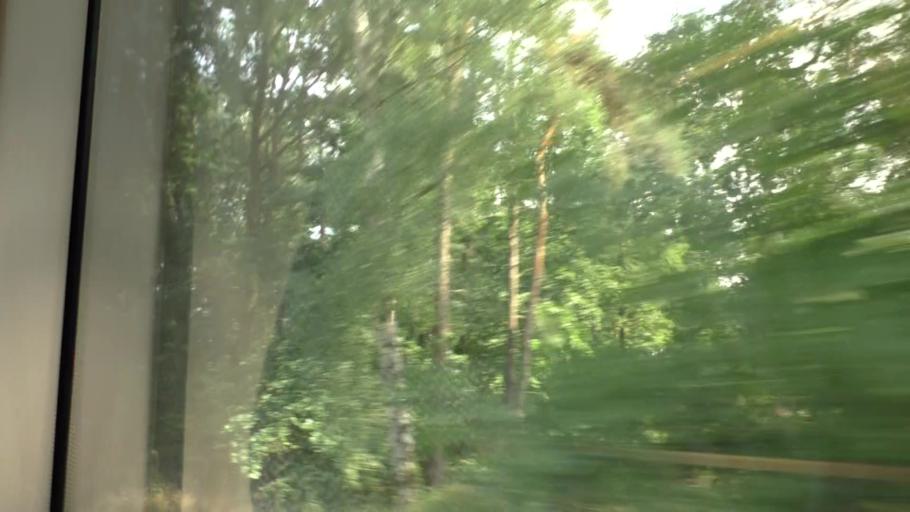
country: DE
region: Brandenburg
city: Bestensee
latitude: 52.3005
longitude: 13.7172
